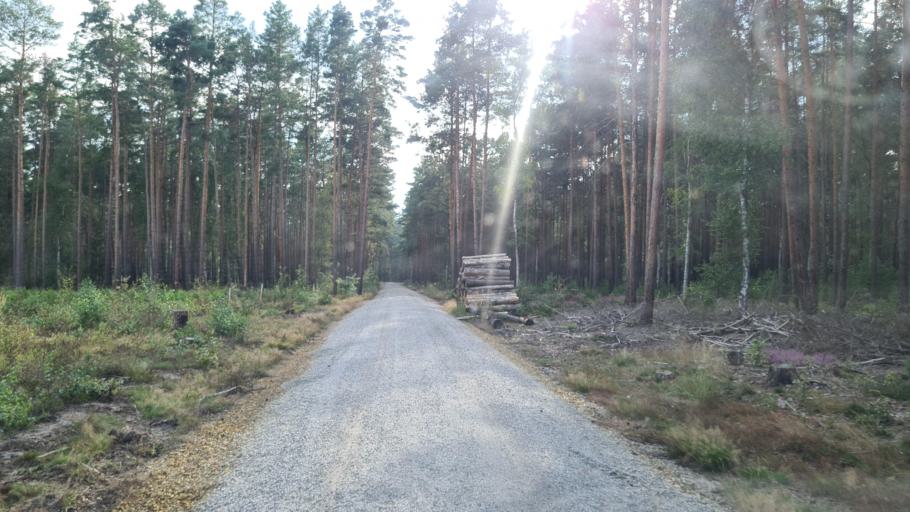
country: DE
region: Brandenburg
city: Schonborn
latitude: 51.6248
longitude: 13.5068
